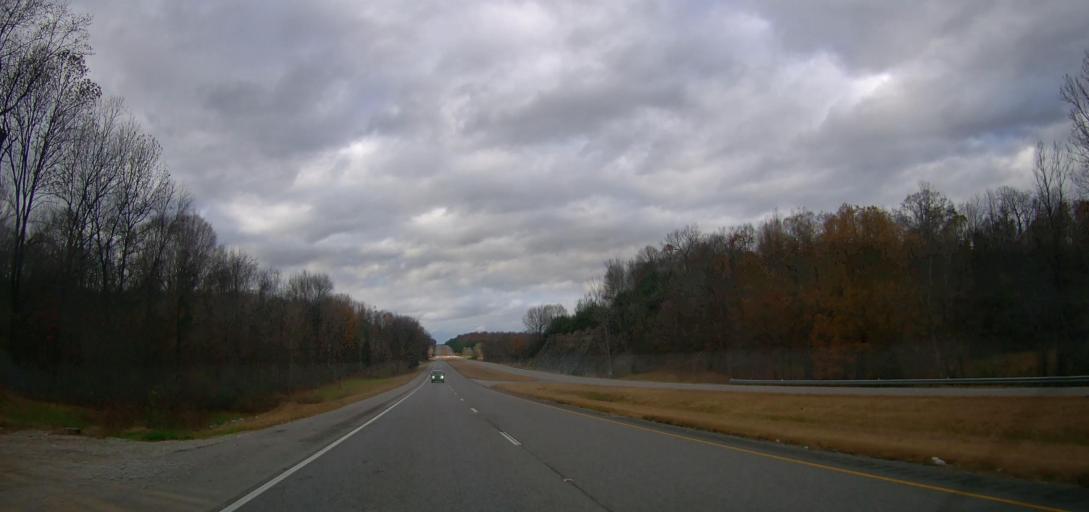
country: US
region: Alabama
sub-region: Lawrence County
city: Town Creek
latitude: 34.6049
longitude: -87.4501
